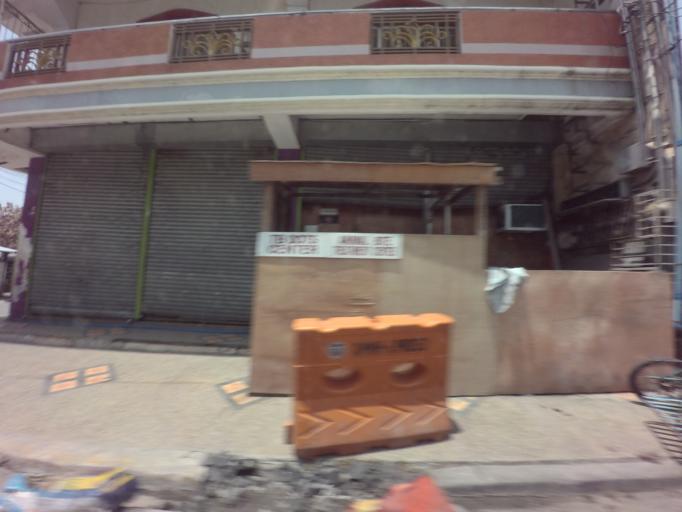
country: PH
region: Calabarzon
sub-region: Province of Laguna
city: San Pedro
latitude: 14.3899
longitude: 121.0481
